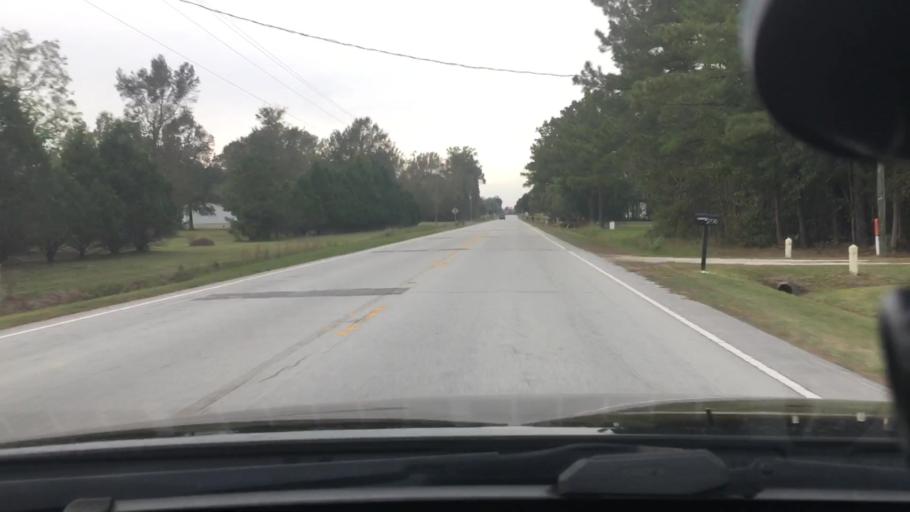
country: US
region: North Carolina
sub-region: Craven County
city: Vanceboro
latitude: 35.3594
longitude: -77.1961
